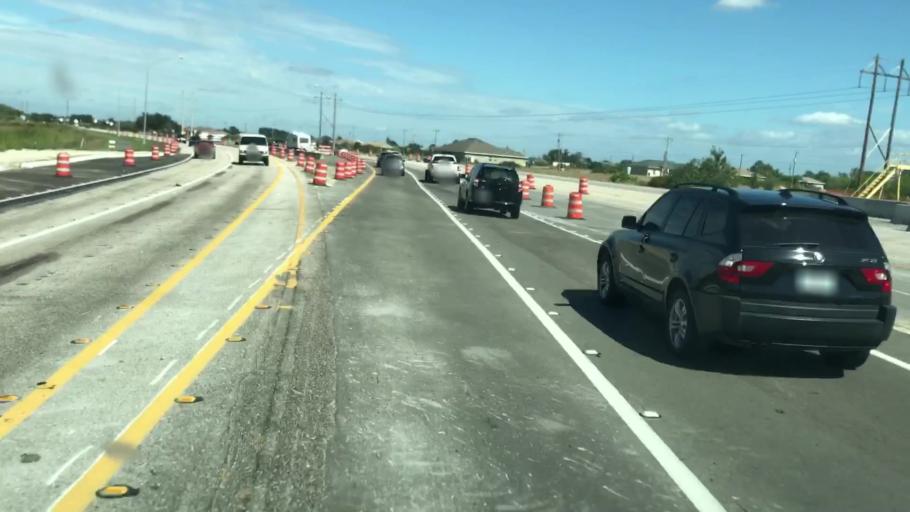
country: US
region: Florida
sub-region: Lee County
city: Gateway
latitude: 26.5837
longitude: -81.7129
